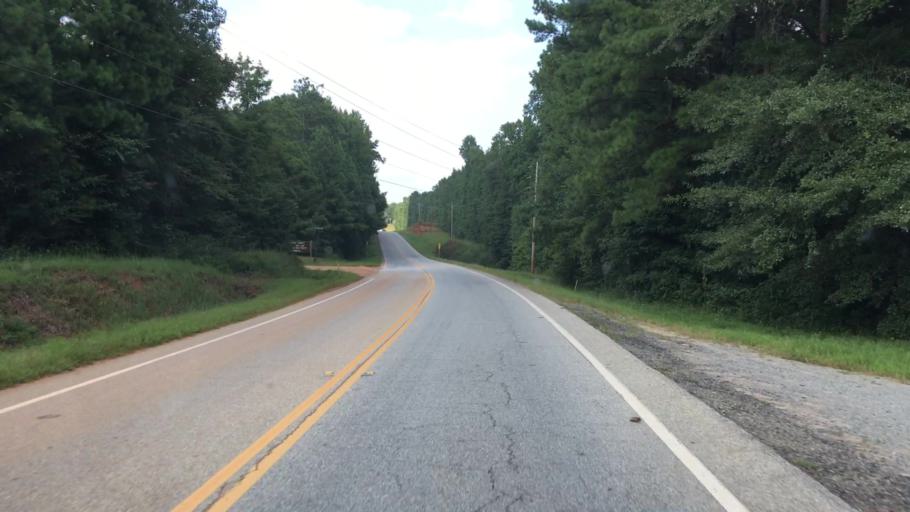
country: US
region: Georgia
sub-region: Monroe County
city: Forsyth
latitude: 33.0806
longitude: -83.9102
